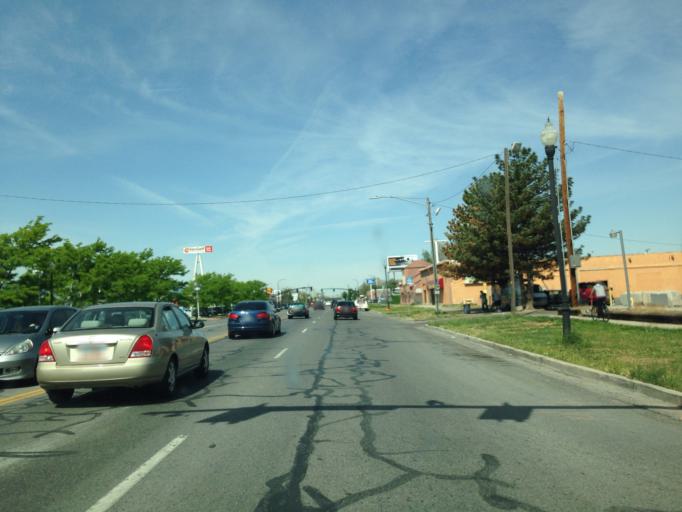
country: US
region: Utah
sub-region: Salt Lake County
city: Salt Lake City
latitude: 40.7498
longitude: -111.8884
